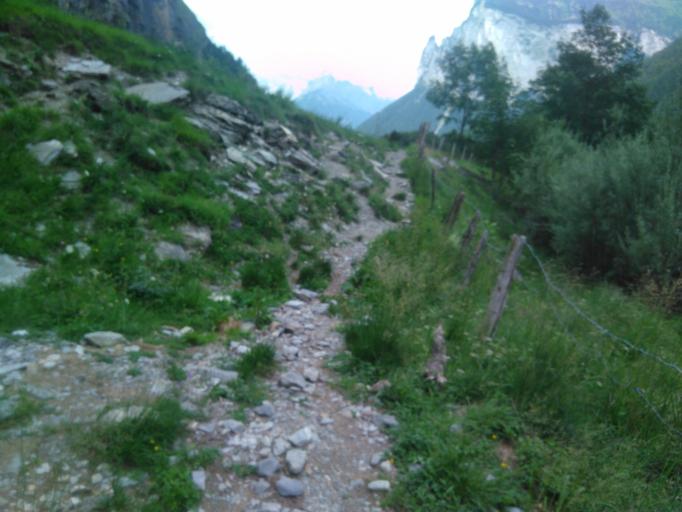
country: CH
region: Bern
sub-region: Interlaken-Oberhasli District
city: Meiringen
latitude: 46.6860
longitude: 8.2092
